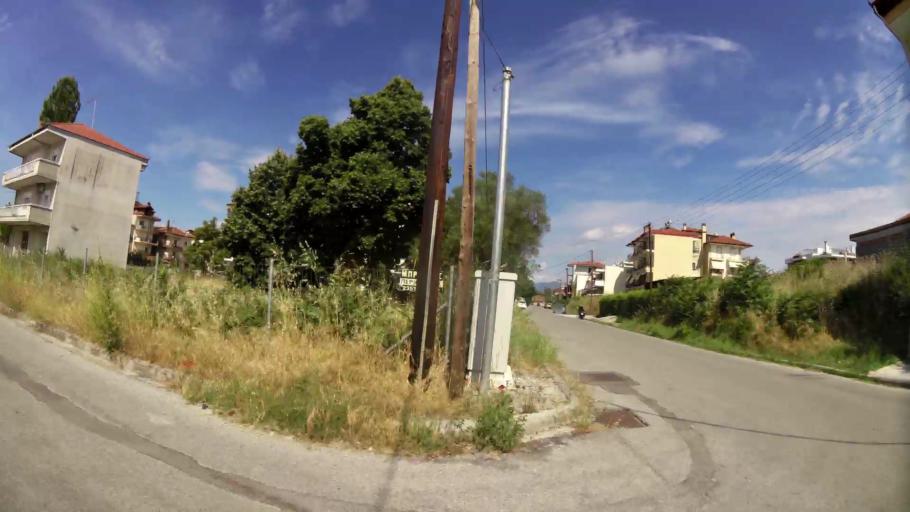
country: GR
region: Central Macedonia
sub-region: Nomos Pierias
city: Katerini
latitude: 40.2744
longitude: 22.4870
